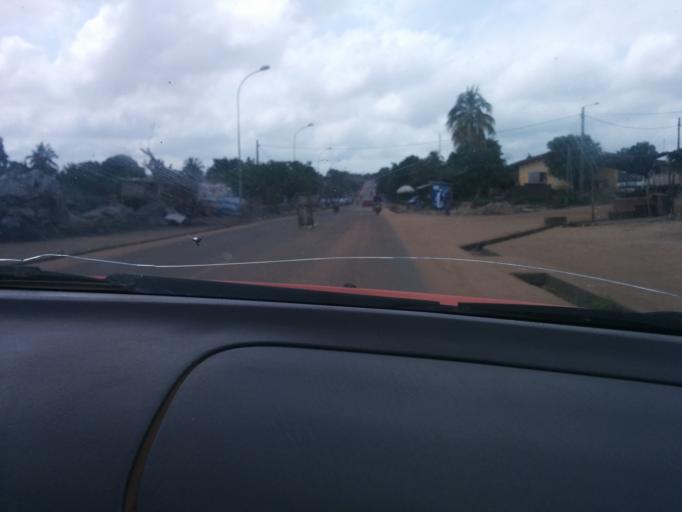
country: CI
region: Vallee du Bandama
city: Bouake
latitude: 7.6947
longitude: -5.0391
